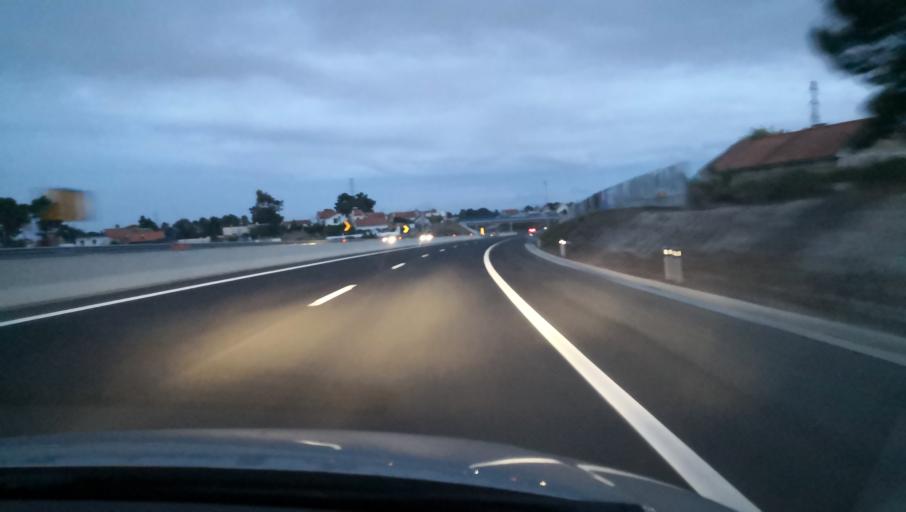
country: PT
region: Setubal
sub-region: Seixal
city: Aldeia de Paio Pires
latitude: 38.5884
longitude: -9.0858
